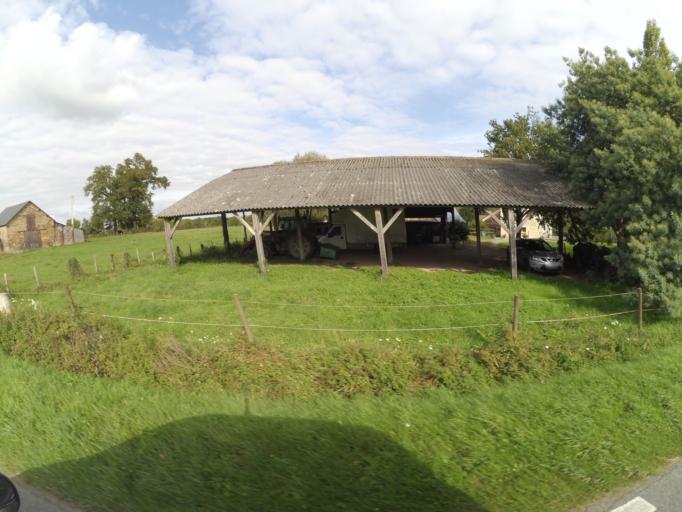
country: FR
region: Pays de la Loire
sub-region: Departement de la Loire-Atlantique
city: Plesse
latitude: 47.5227
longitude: -1.8956
